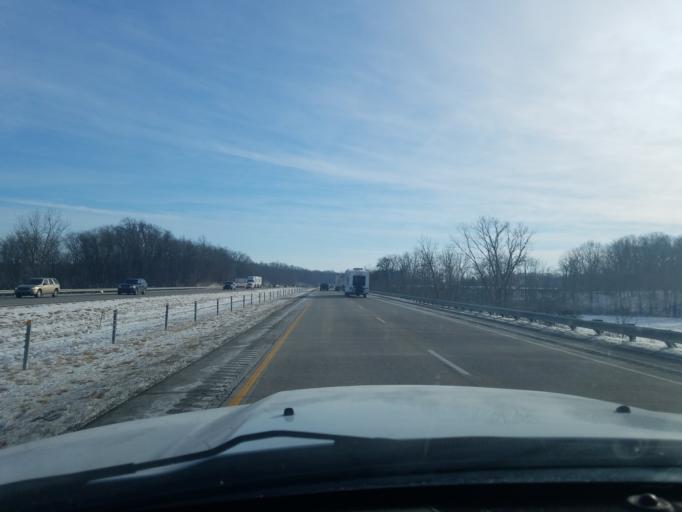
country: US
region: Indiana
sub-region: Grant County
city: Upland
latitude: 40.4504
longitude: -85.5477
